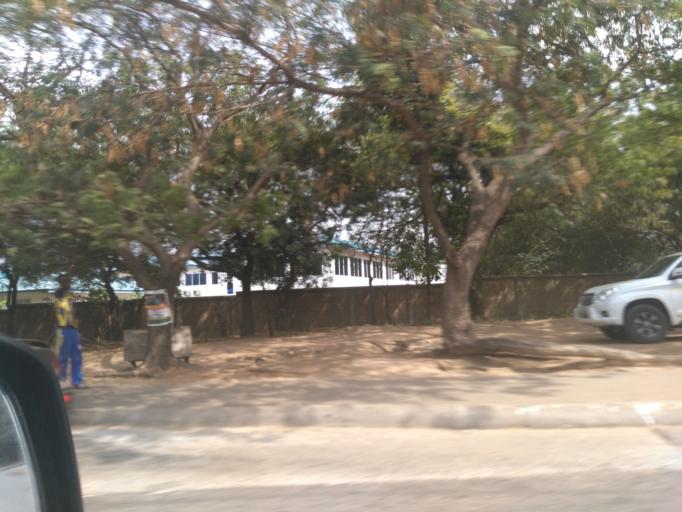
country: GH
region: Greater Accra
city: Accra
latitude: 5.5937
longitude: -0.1858
